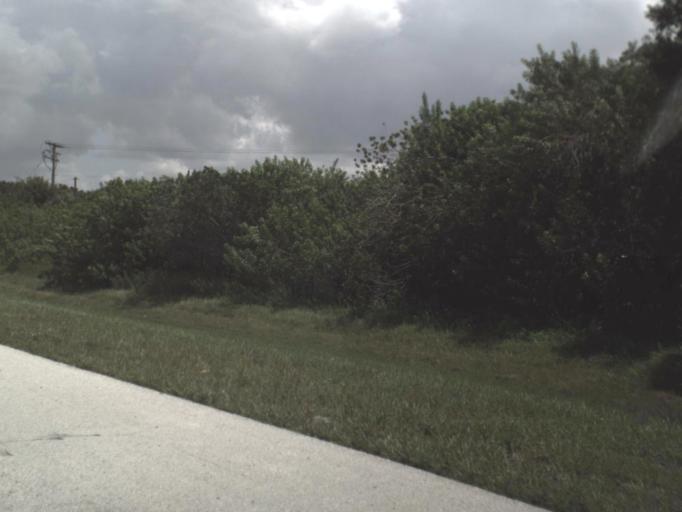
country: US
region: Florida
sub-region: Hillsborough County
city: Sun City Center
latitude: 27.7044
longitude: -82.3910
